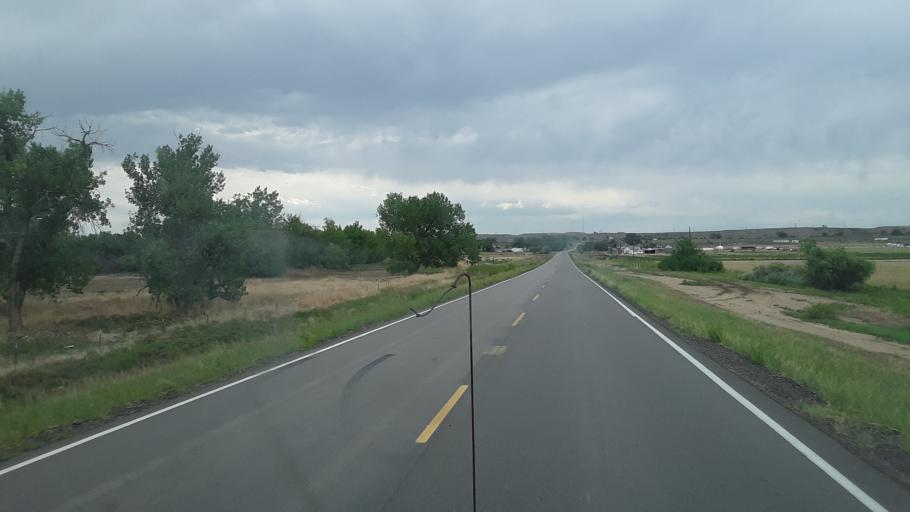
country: US
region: Colorado
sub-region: Otero County
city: Fowler
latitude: 38.1425
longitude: -104.0227
